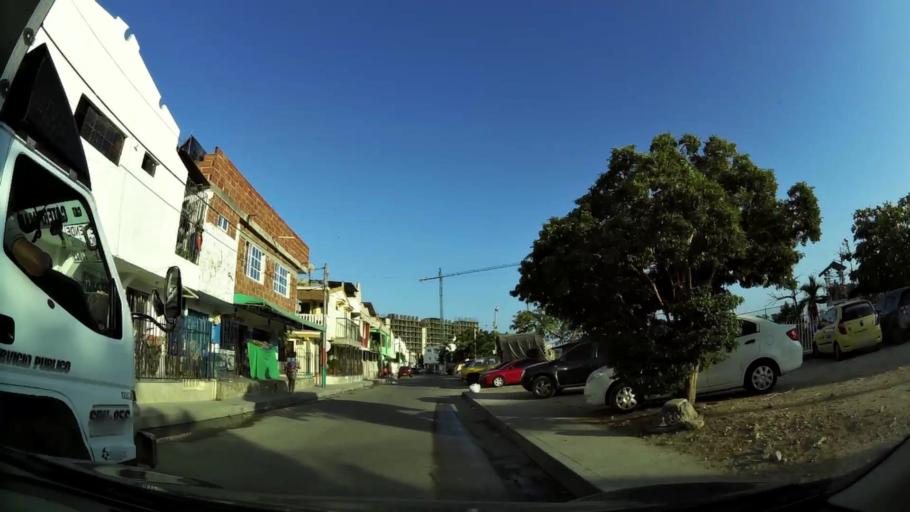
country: CO
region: Bolivar
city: Cartagena
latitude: 10.4001
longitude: -75.4721
